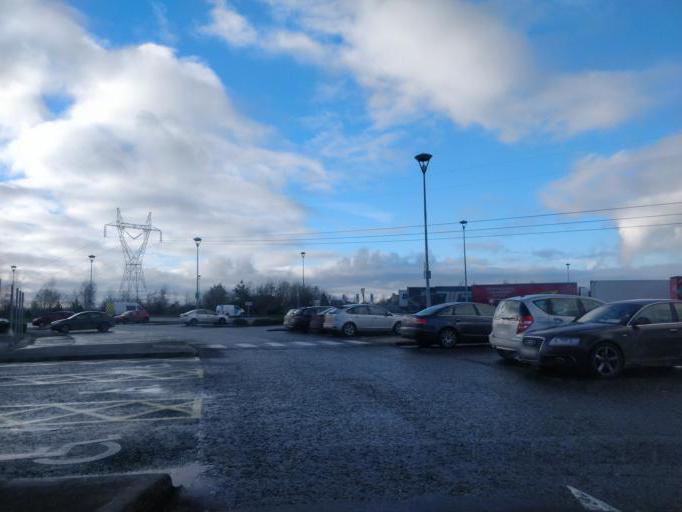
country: IE
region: Leinster
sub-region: An Mhi
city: Enfield
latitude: 53.4137
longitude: -6.8819
